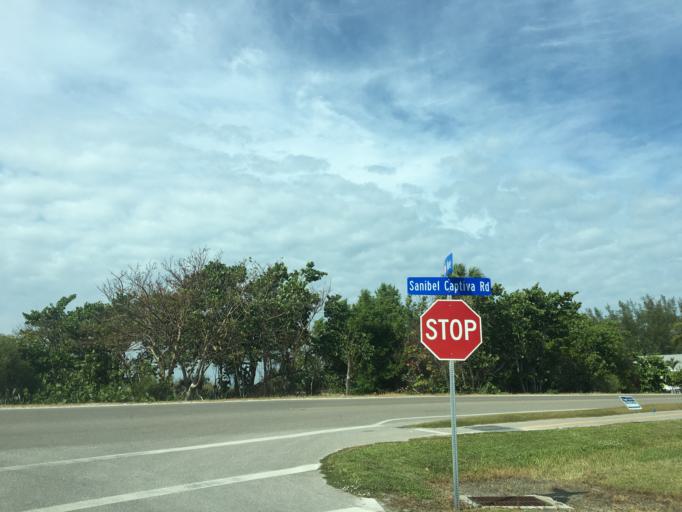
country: US
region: Florida
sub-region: Lee County
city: Saint James City
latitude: 26.4798
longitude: -82.1805
